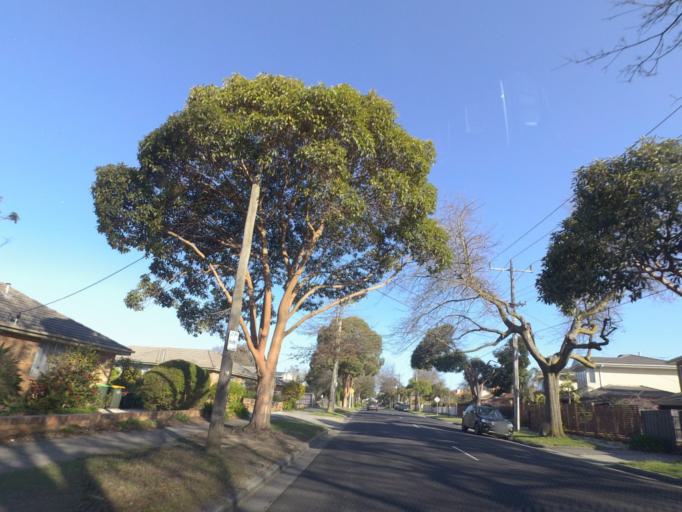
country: AU
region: Victoria
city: Mitcham
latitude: -37.8126
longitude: 145.1951
